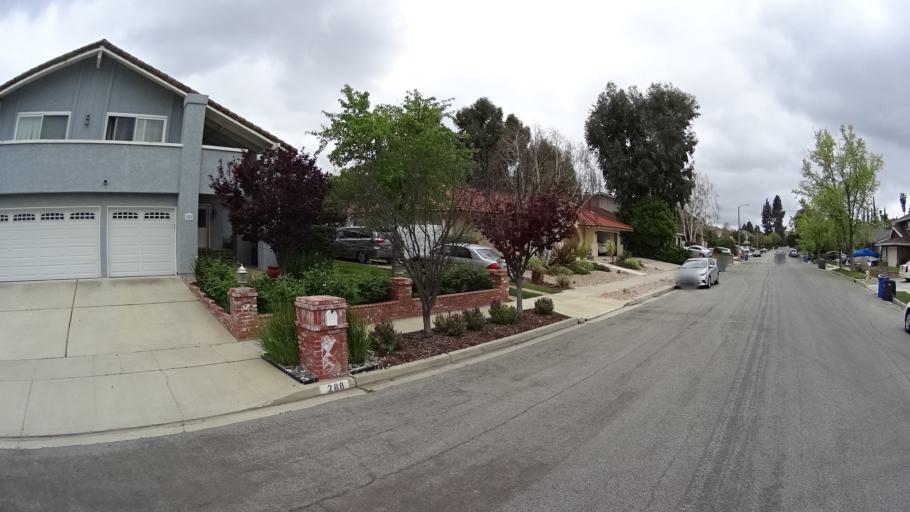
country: US
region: California
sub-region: Ventura County
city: Thousand Oaks
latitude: 34.2106
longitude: -118.8831
